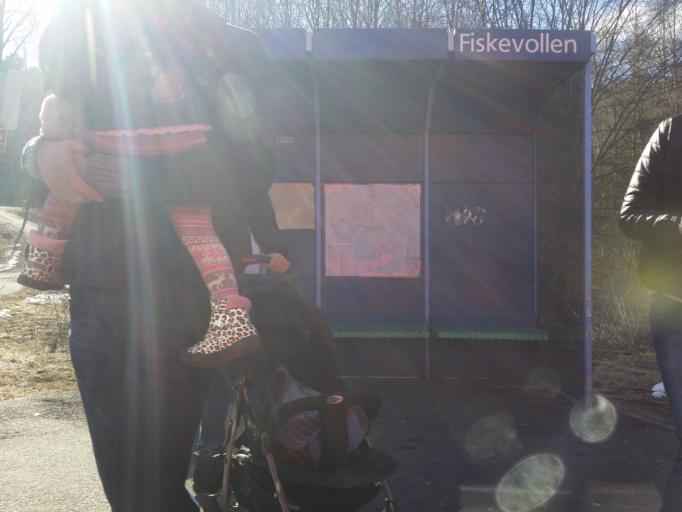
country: NO
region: Akershus
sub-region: Oppegard
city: Kolbotn
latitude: 59.8406
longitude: 10.7781
